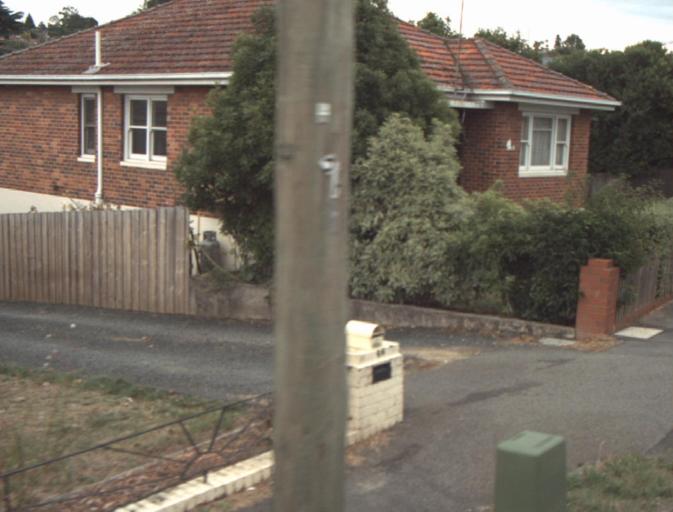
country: AU
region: Tasmania
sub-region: Launceston
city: East Launceston
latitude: -41.4622
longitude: 147.1566
